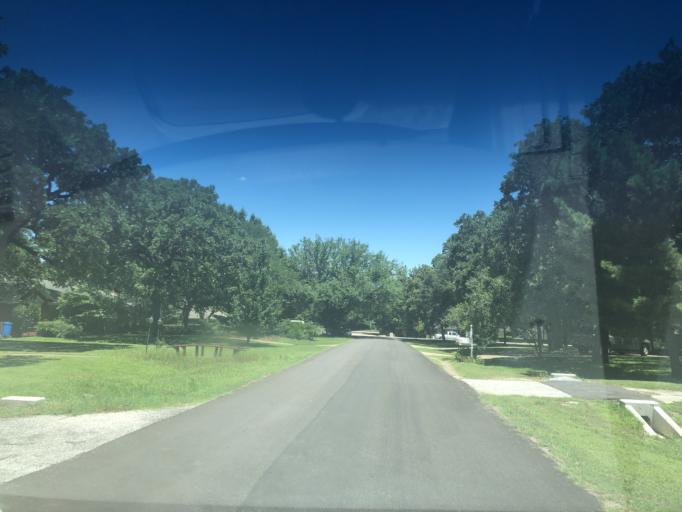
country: US
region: Texas
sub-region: Dallas County
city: Grand Prairie
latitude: 32.7790
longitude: -97.0344
